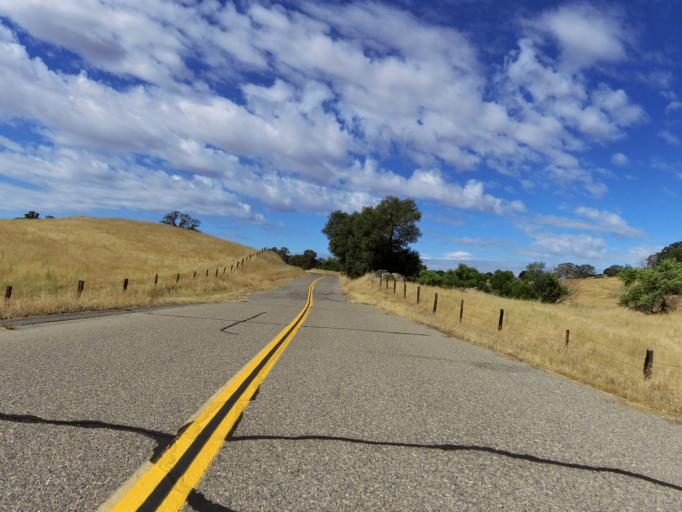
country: US
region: California
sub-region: Madera County
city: Yosemite Lakes
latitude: 37.0563
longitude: -119.7400
